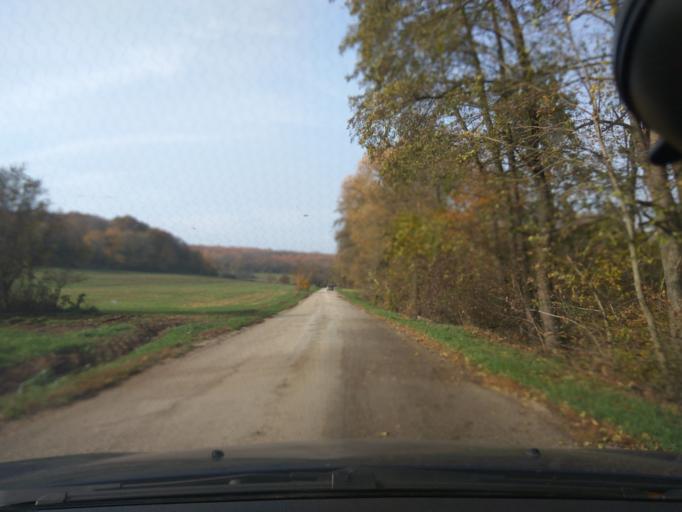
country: SK
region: Nitriansky
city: Cachtice
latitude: 48.6673
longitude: 17.7540
